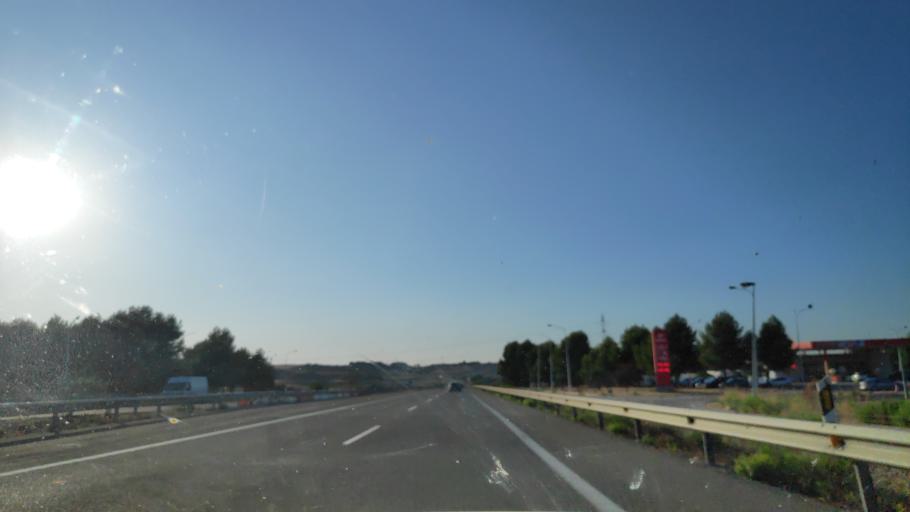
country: ES
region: Castille-La Mancha
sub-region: Provincia de Cuenca
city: Belinchon
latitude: 40.0319
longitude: -3.0407
